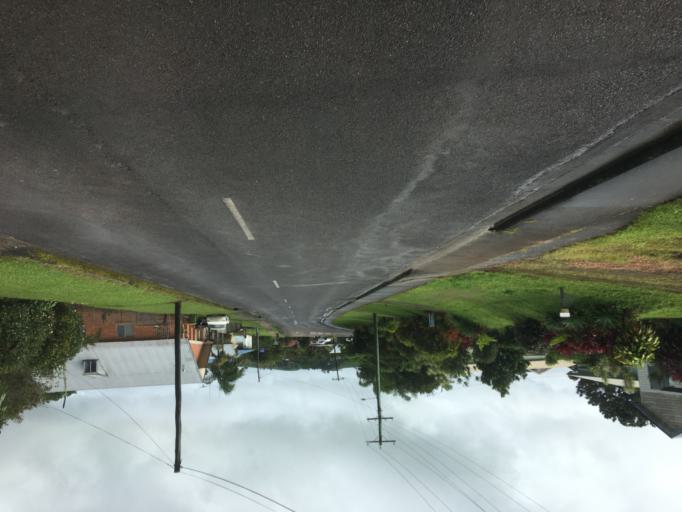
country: AU
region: Queensland
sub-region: Tablelands
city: Ravenshoe
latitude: -17.5125
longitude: 145.6113
